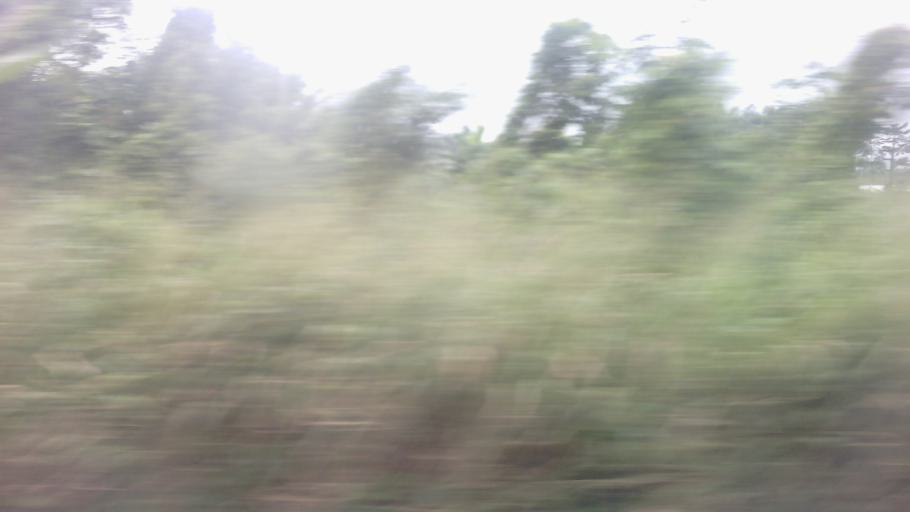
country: CI
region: Sud-Comoe
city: Aboisso
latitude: 5.4112
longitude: -3.2870
